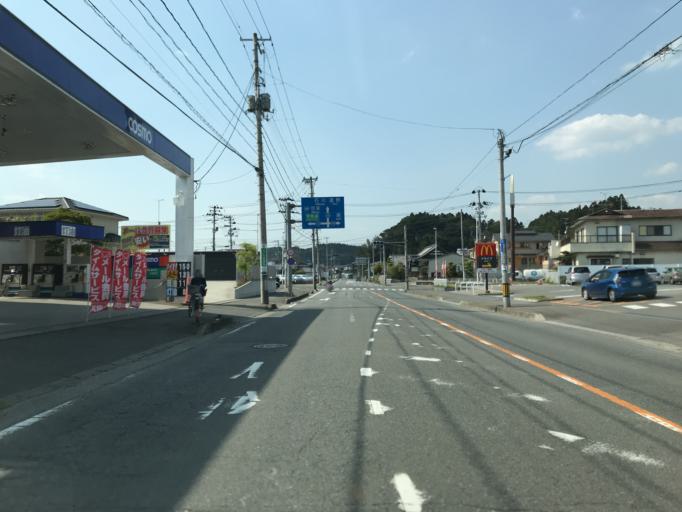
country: JP
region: Ibaraki
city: Kitaibaraki
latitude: 36.9216
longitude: 140.7863
